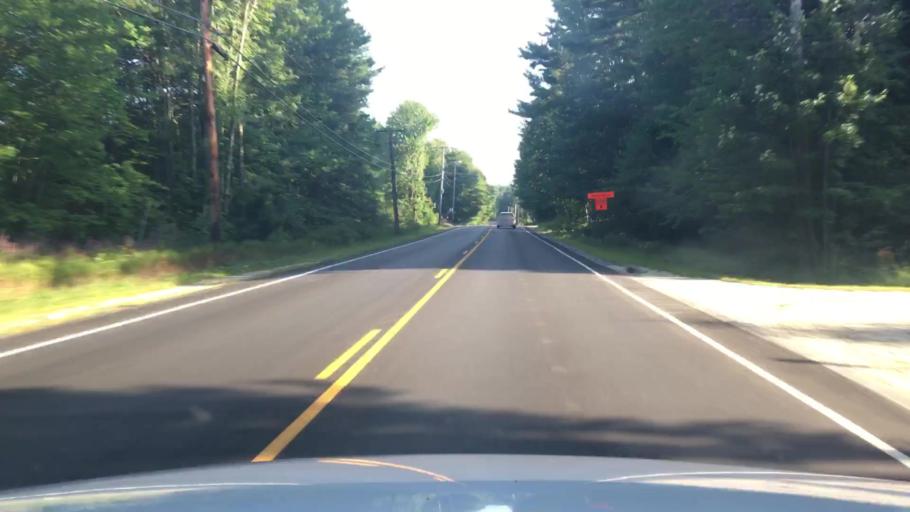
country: US
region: Maine
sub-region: Cumberland County
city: Cumberland Center
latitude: 43.8387
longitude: -70.3214
